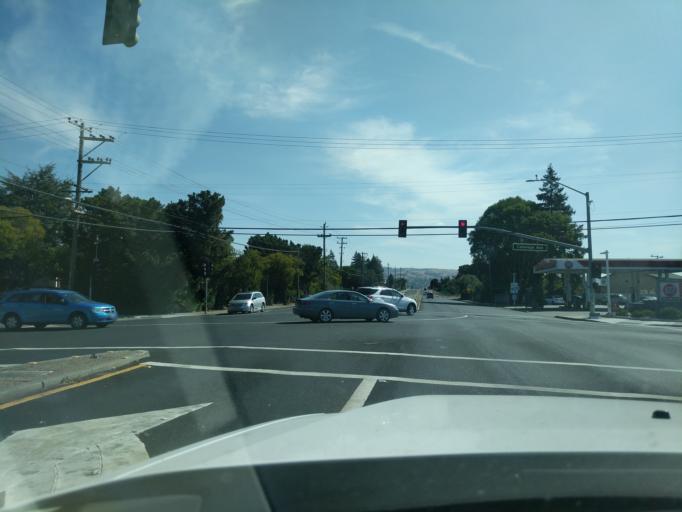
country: US
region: California
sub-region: Alameda County
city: Hayward
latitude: 37.6316
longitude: -122.0900
